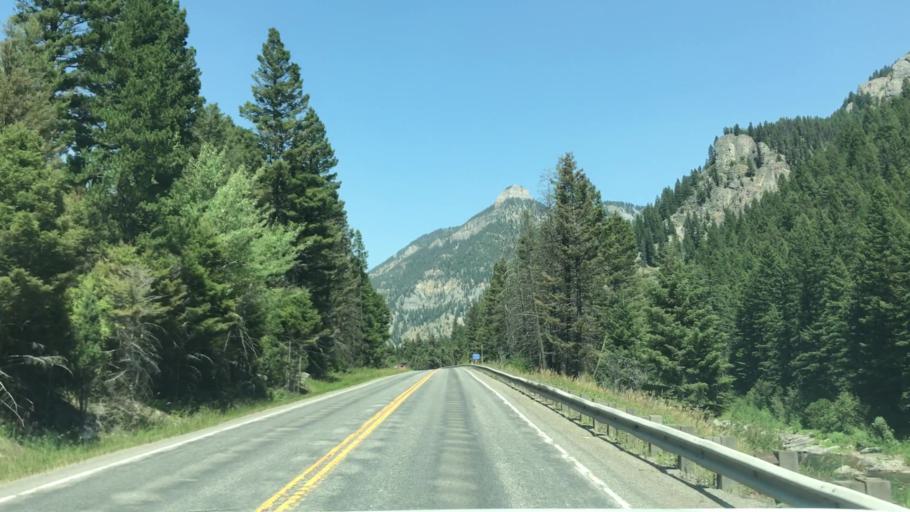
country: US
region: Montana
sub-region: Gallatin County
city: Big Sky
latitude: 45.4262
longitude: -111.2335
